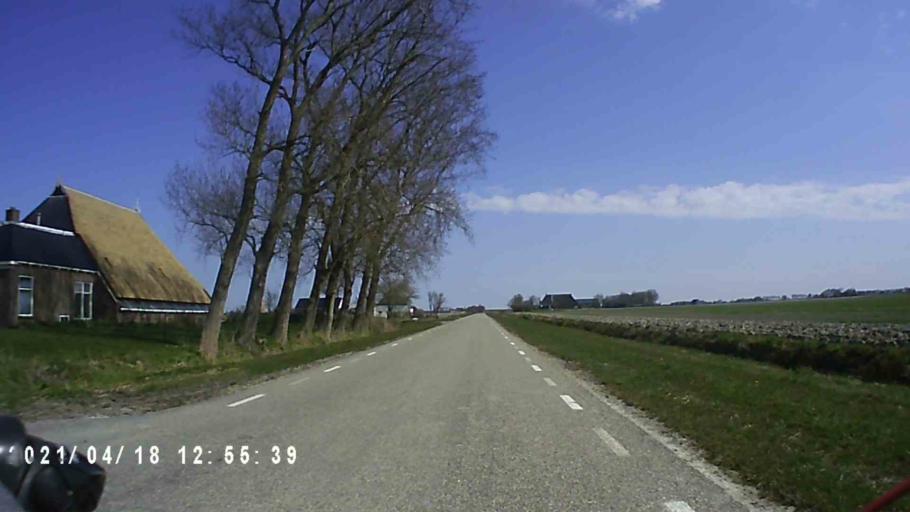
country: NL
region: Friesland
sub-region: Gemeente Dongeradeel
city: Anjum
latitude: 53.3876
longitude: 6.0748
